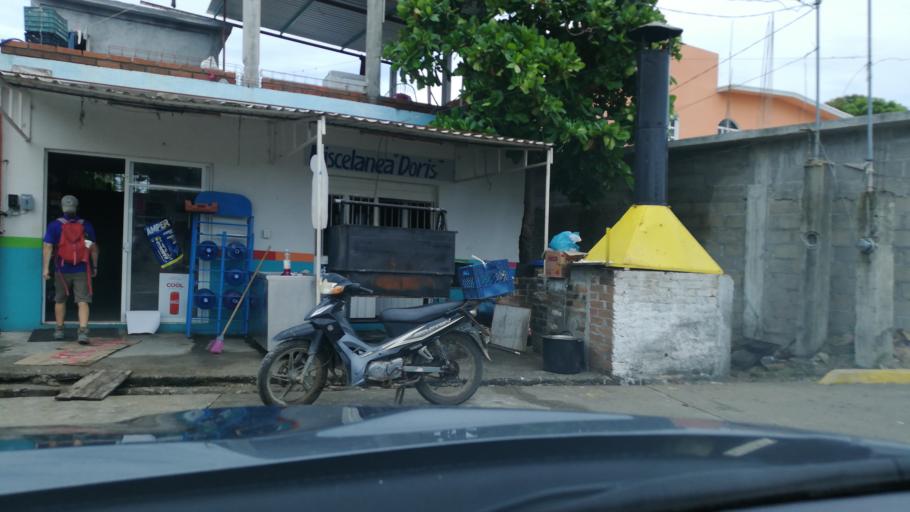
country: MX
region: Oaxaca
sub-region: Salina Cruz
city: Salina Cruz
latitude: 16.1634
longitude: -95.2201
